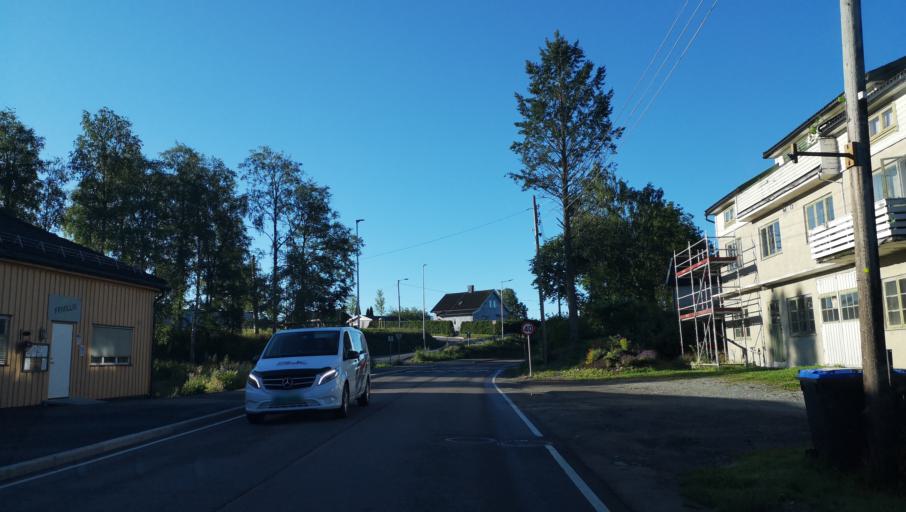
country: NO
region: Ostfold
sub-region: Hobol
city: Tomter
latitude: 59.6587
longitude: 11.0009
